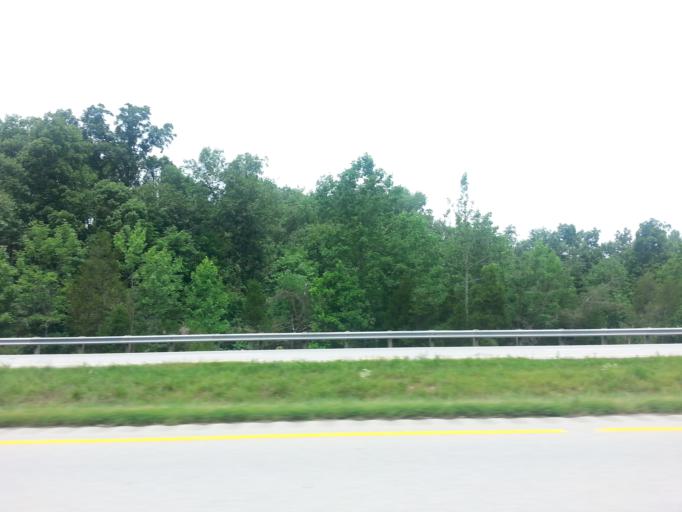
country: US
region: Kentucky
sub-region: Grayson County
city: Leitchfield
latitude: 37.5569
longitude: -86.0780
